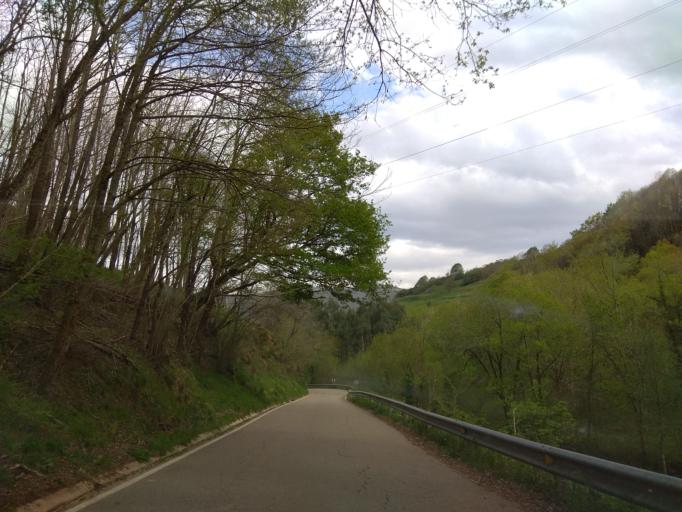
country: ES
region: Cantabria
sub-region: Provincia de Cantabria
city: Cabezon de Liebana
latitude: 43.2537
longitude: -4.4930
